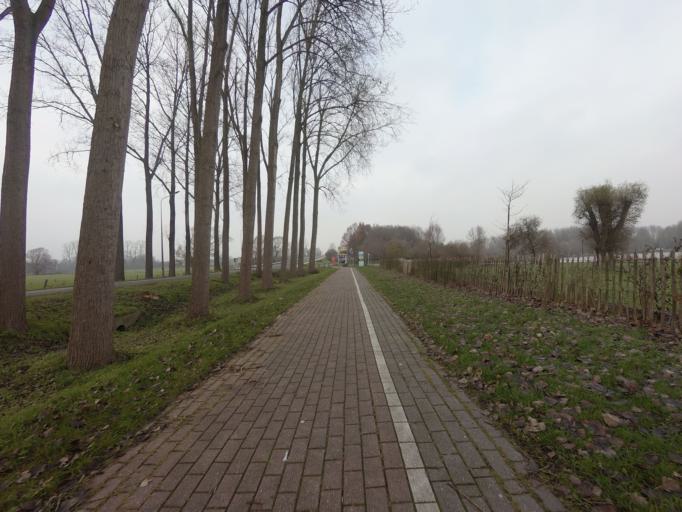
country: BE
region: Flanders
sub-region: Provincie Oost-Vlaanderen
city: Geraardsbergen
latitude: 50.7910
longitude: 3.9043
